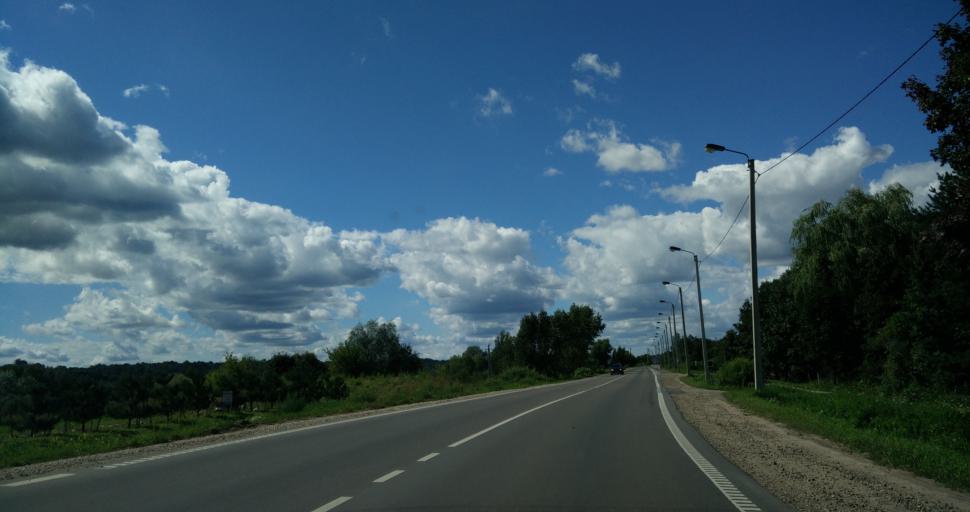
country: LT
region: Kauno apskritis
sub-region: Kauno rajonas
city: Akademija (Kaunas)
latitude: 54.9208
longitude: 23.8022
